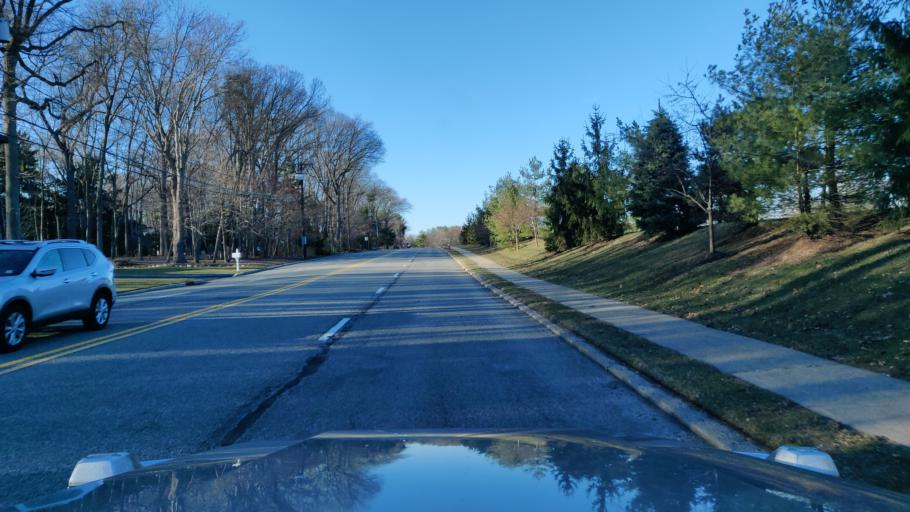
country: US
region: New Jersey
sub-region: Bergen County
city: Woodcliff Lake
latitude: 41.0301
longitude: -74.0741
